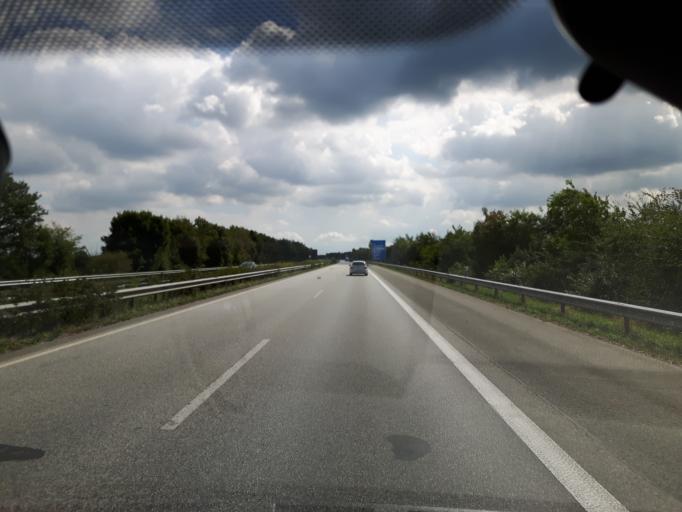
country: DE
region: Schleswig-Holstein
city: Handewitt
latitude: 54.7801
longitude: 9.3413
